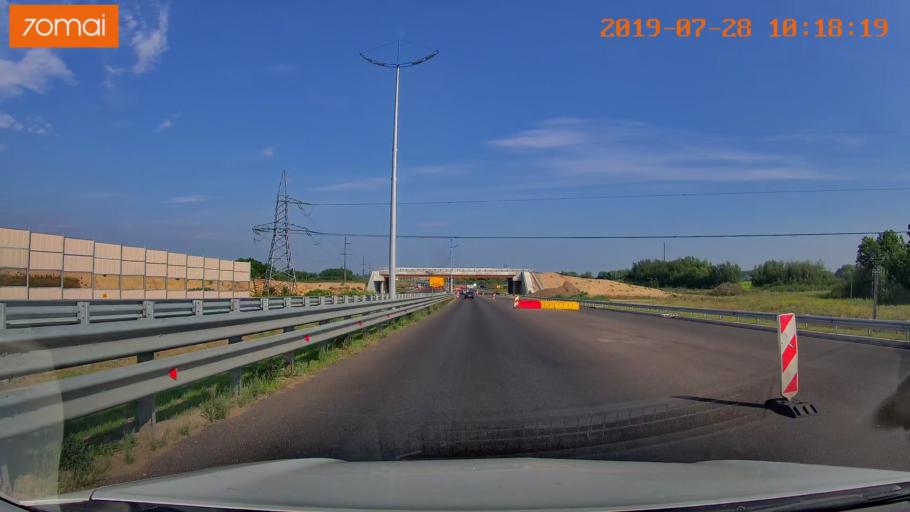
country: RU
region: Kaliningrad
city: Maloye Isakovo
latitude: 54.7506
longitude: 20.5886
